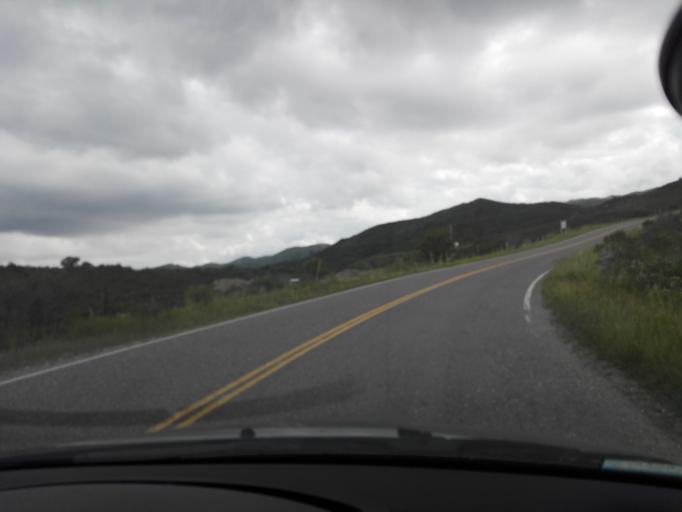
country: AR
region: Cordoba
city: Alta Gracia
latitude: -31.5912
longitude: -64.5096
